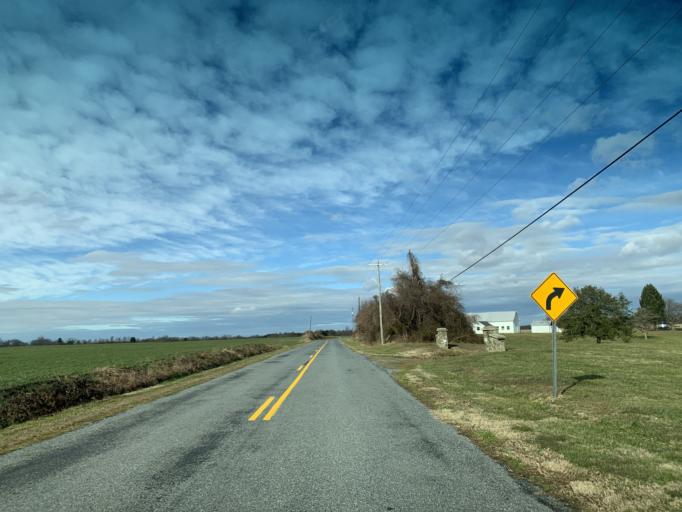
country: US
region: Maryland
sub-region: Kent County
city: Chestertown
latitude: 39.3427
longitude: -76.0516
